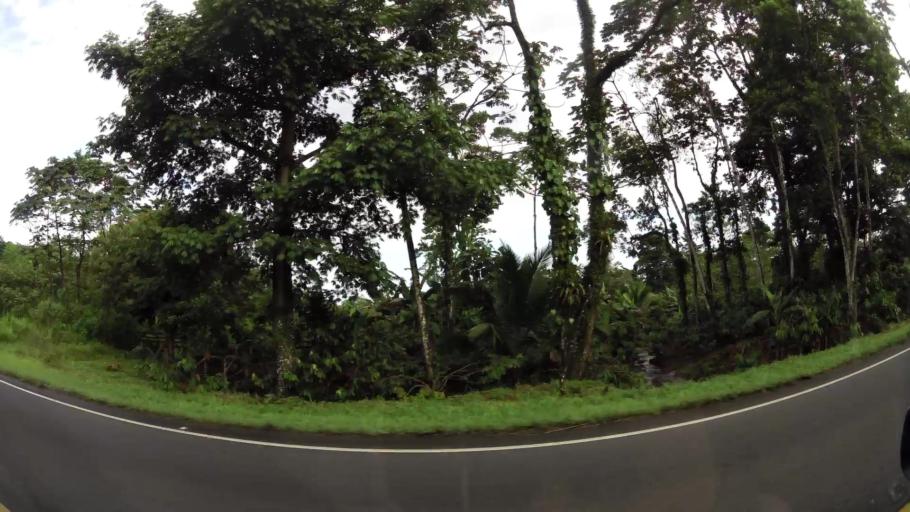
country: CR
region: Limon
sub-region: Canton de Guacimo
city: Guacimo
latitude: 10.2048
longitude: -83.7173
